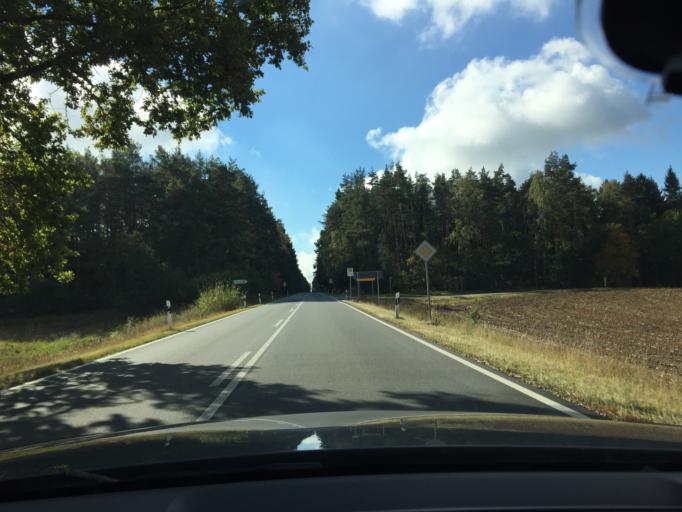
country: DE
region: Mecklenburg-Vorpommern
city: Krakow am See
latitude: 53.6340
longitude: 12.2554
